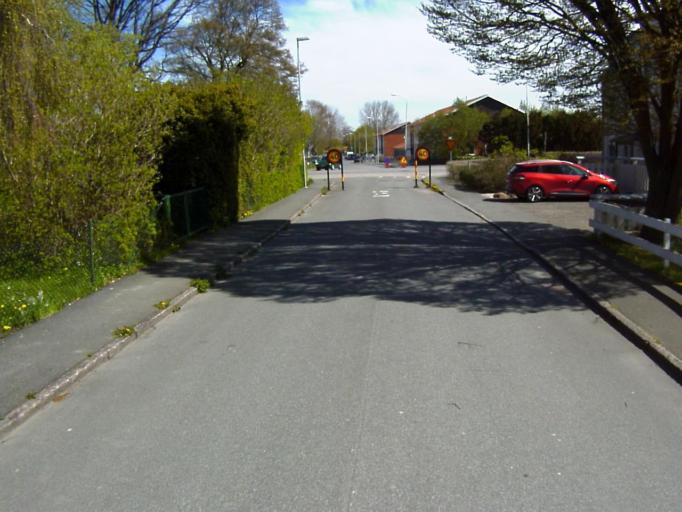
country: SE
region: Skane
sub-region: Kristianstads Kommun
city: Kristianstad
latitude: 56.0501
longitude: 14.1542
